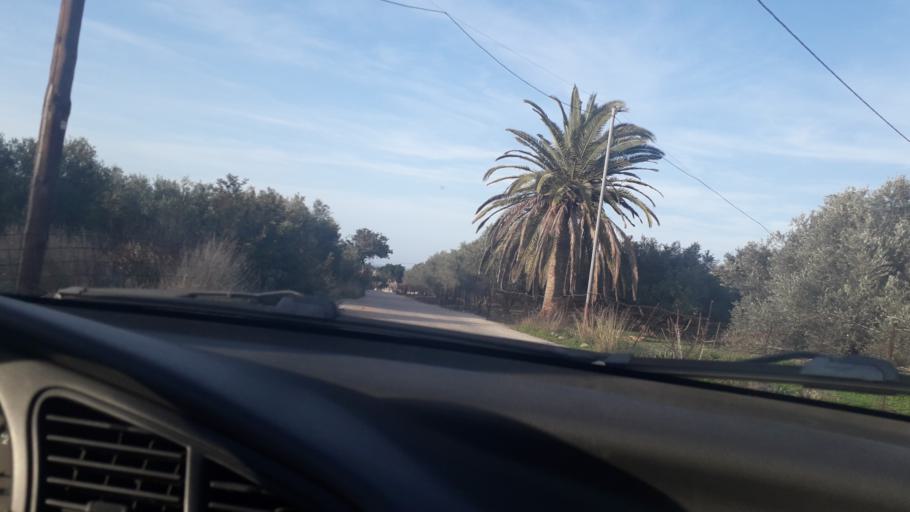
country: GR
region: Crete
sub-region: Nomos Rethymnis
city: Panormos
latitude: 35.3860
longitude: 24.6243
